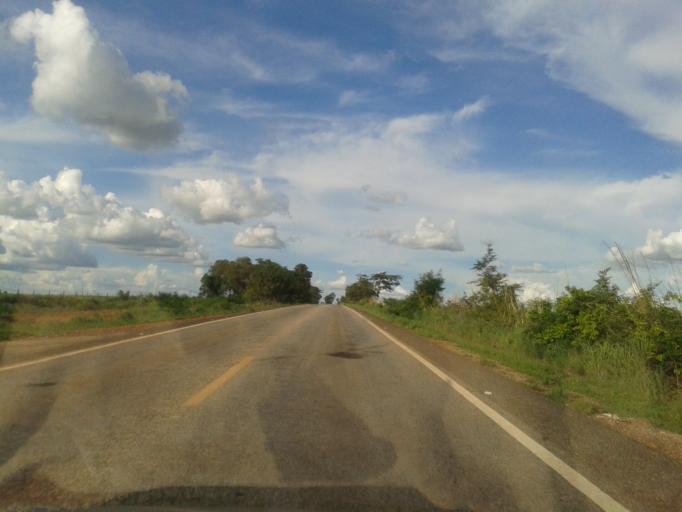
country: BR
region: Goias
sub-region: Mozarlandia
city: Mozarlandia
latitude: -14.5361
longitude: -50.4879
